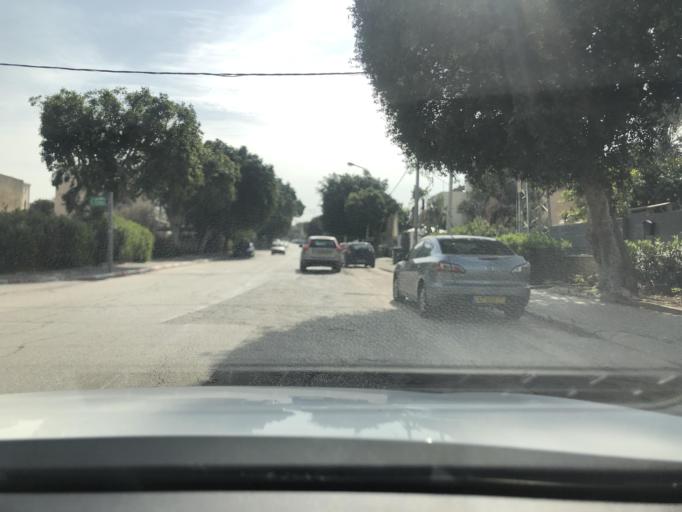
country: IL
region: Central District
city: Rosh Ha'Ayin
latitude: 32.0922
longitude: 34.9471
